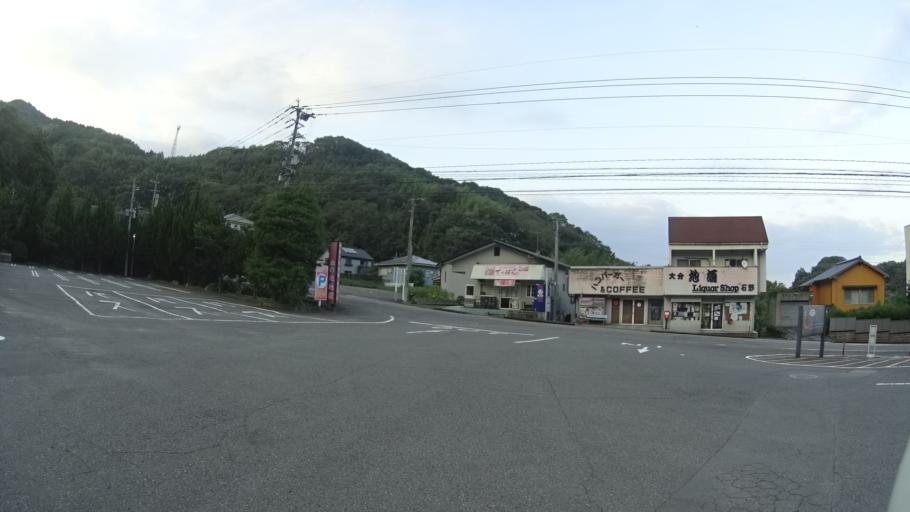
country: JP
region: Oita
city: Beppu
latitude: 33.3275
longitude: 131.4788
